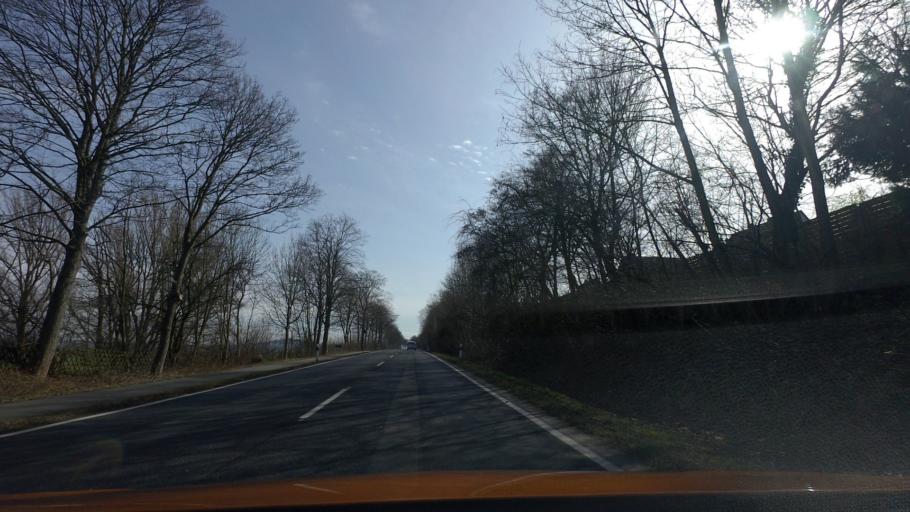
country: DE
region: Lower Saxony
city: Beckedorf
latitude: 52.3383
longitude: 9.3201
